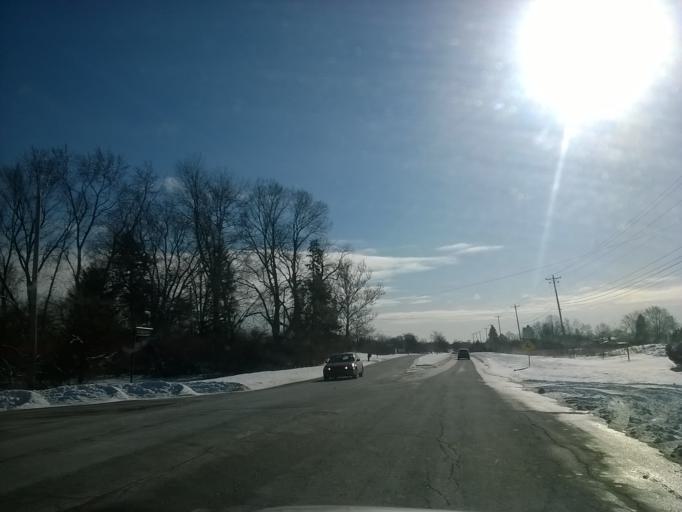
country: US
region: Indiana
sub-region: Hamilton County
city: Carmel
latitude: 39.9344
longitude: -86.1269
